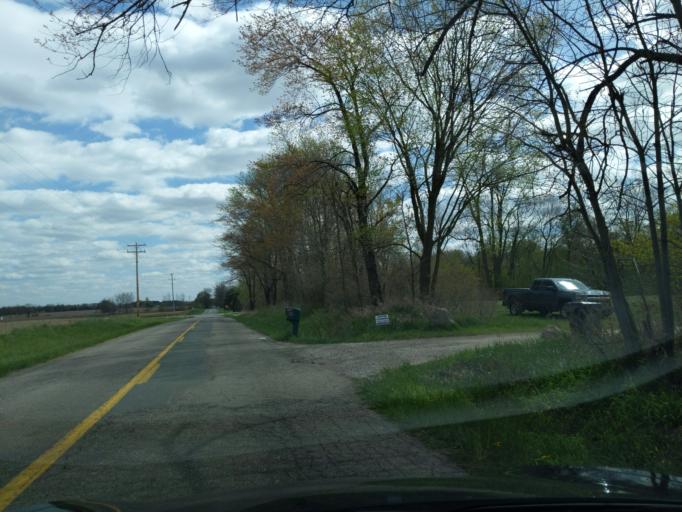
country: US
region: Michigan
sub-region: Ingham County
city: Mason
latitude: 42.5256
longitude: -84.5421
